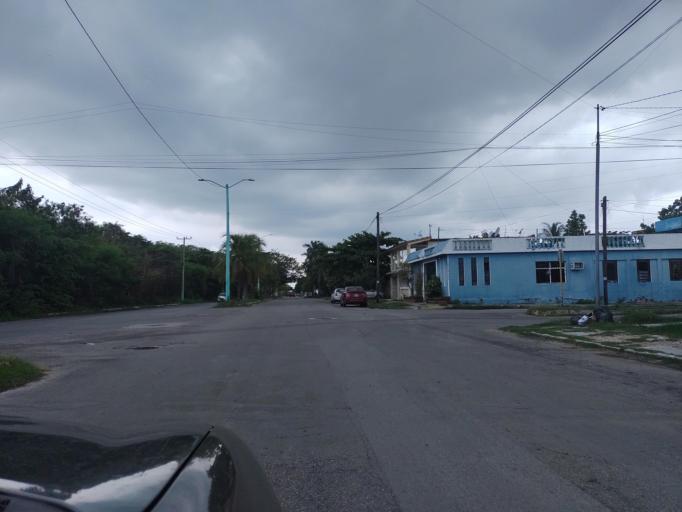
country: MX
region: Quintana Roo
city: Chetumal
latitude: 18.5170
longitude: -88.2778
